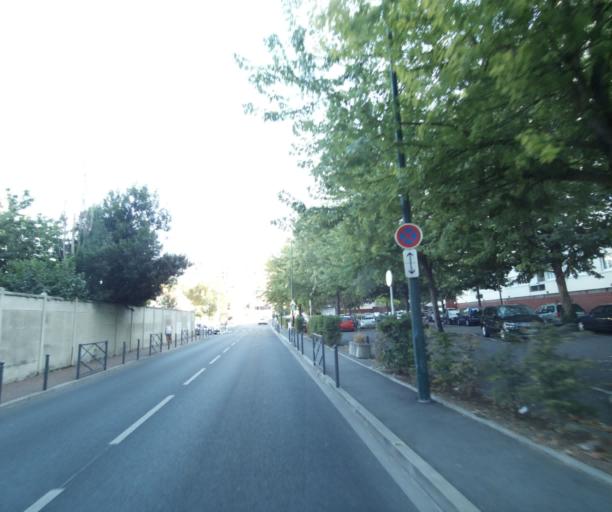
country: FR
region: Ile-de-France
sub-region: Departement des Hauts-de-Seine
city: Villeneuve-la-Garenne
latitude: 48.9393
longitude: 2.3322
